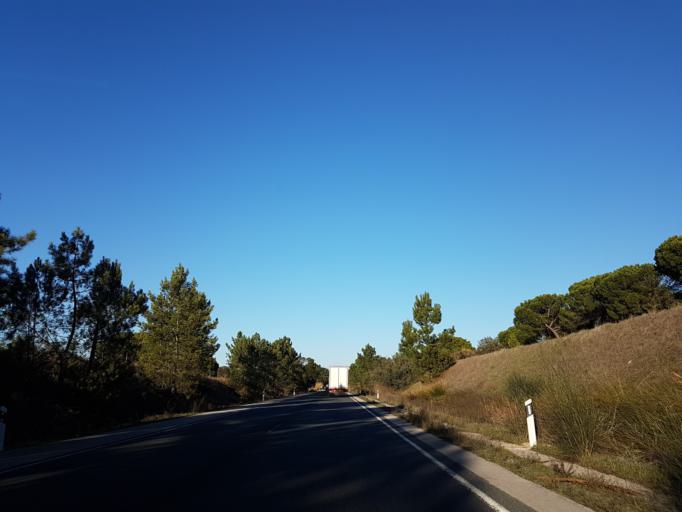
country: PT
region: Setubal
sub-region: Alcacer do Sal
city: Alcacer do Sal
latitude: 38.3985
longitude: -8.5187
